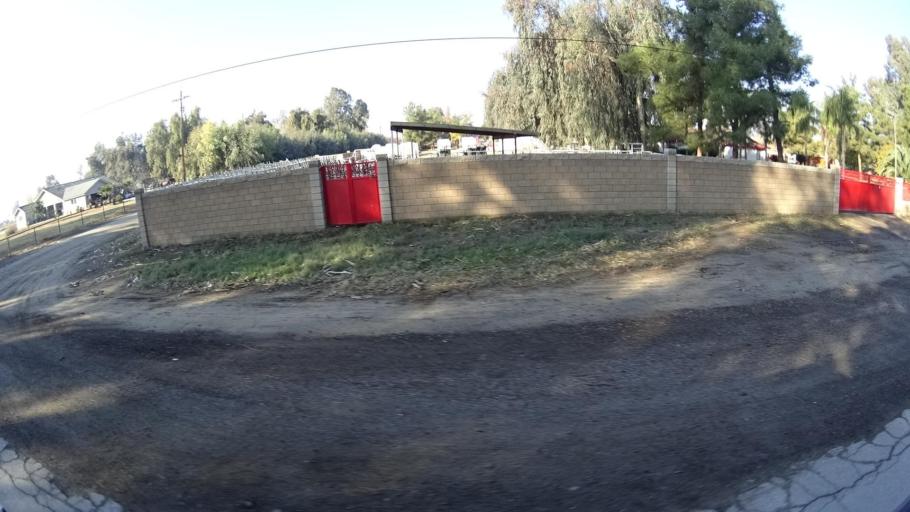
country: US
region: California
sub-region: Kern County
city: Greenfield
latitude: 35.1967
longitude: -119.0027
